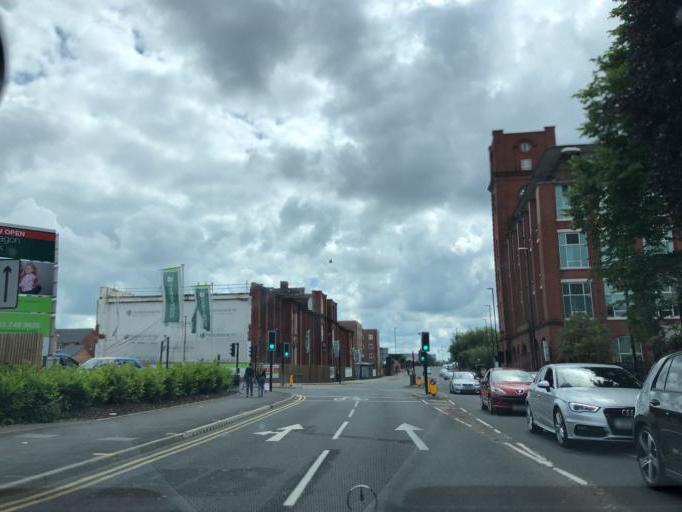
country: GB
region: England
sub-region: Coventry
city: Coventry
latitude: 52.4248
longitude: -1.5023
